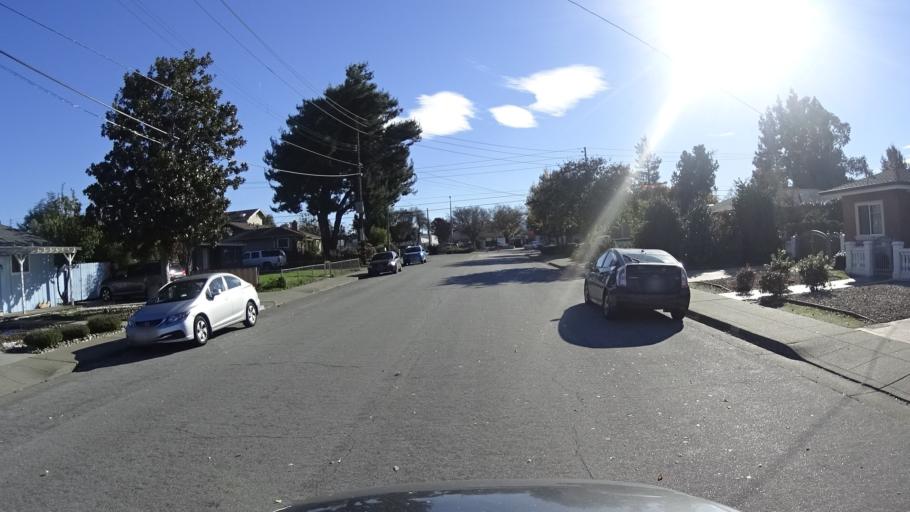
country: US
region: California
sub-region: Santa Clara County
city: Cupertino
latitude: 37.3456
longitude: -122.0263
